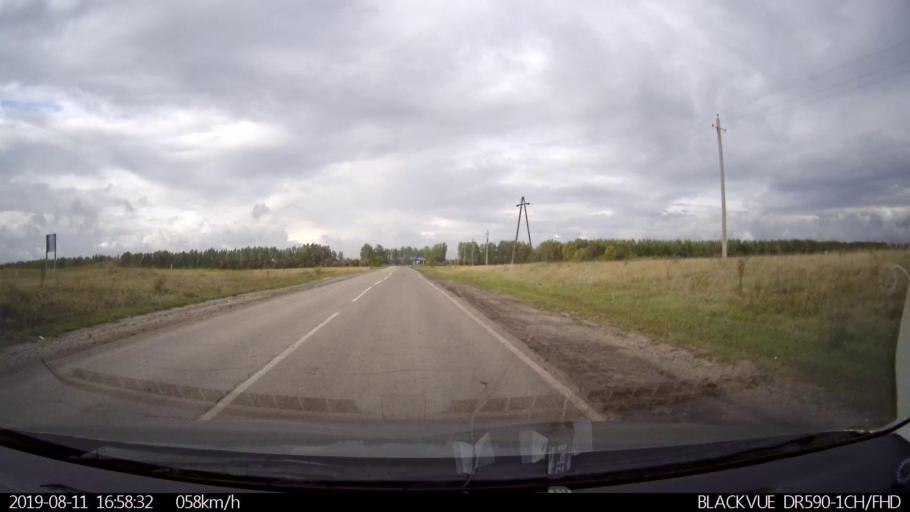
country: RU
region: Ulyanovsk
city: Mayna
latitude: 54.3090
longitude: 47.6564
